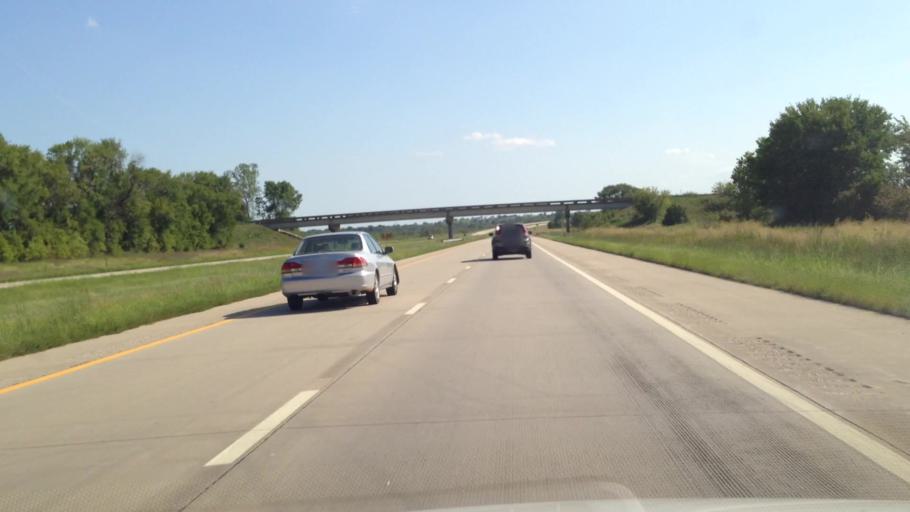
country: US
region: Kansas
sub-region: Bourbon County
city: Fort Scott
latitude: 37.9813
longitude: -94.7045
